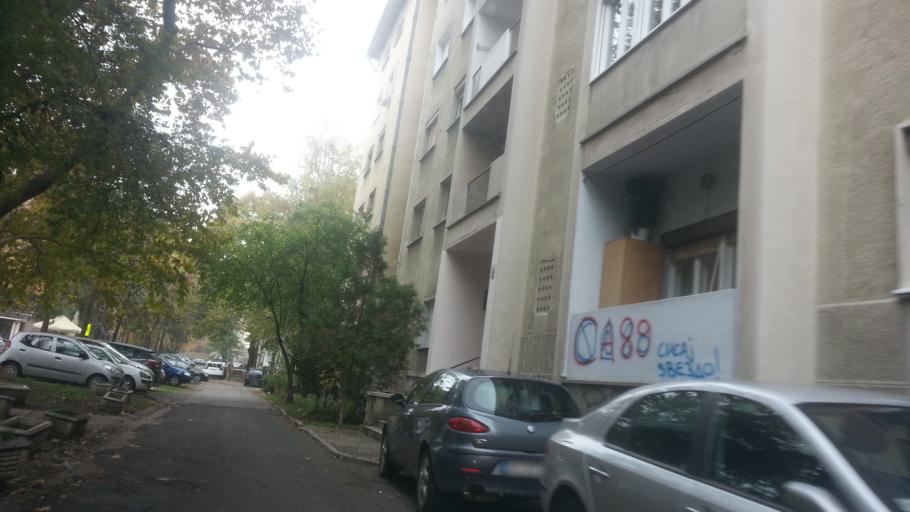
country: RS
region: Central Serbia
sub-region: Belgrade
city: Zemun
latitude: 44.8324
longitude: 20.4061
